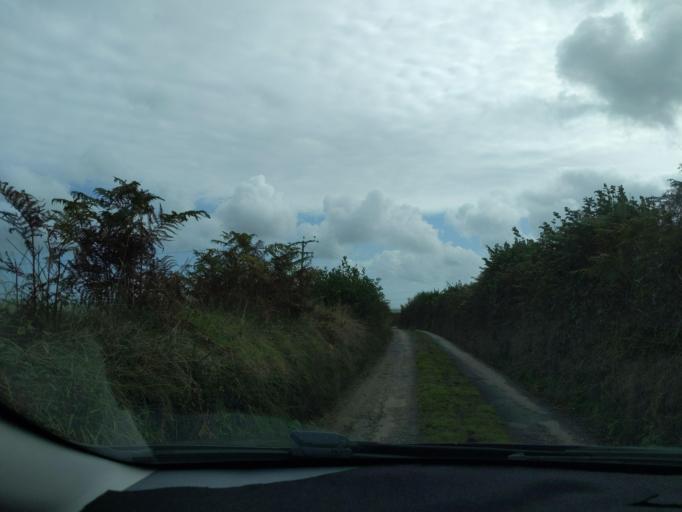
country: GB
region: England
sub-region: Cornwall
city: Par
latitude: 50.3884
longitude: -4.7031
